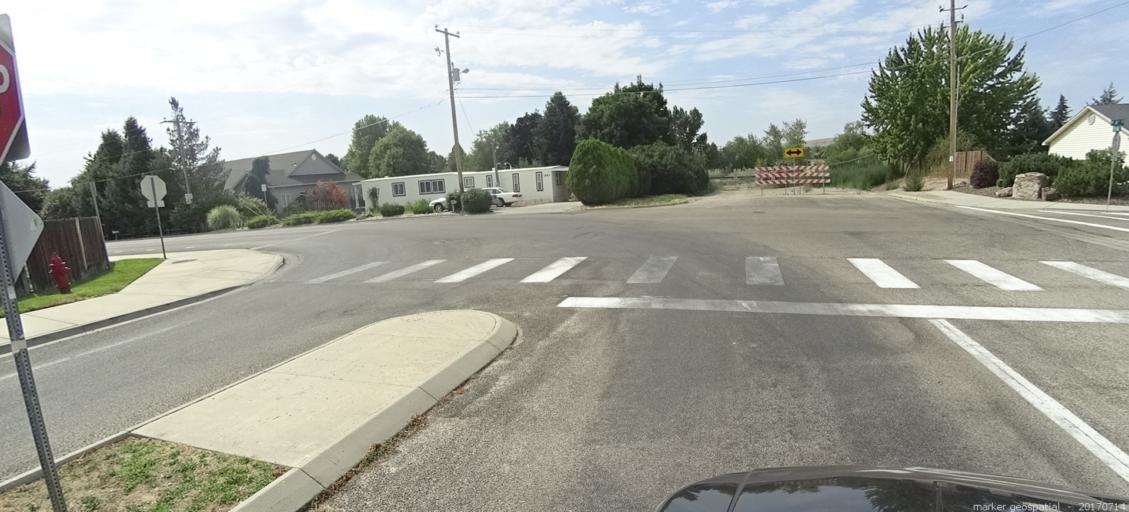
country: US
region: Idaho
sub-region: Ada County
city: Kuna
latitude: 43.4922
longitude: -116.4336
